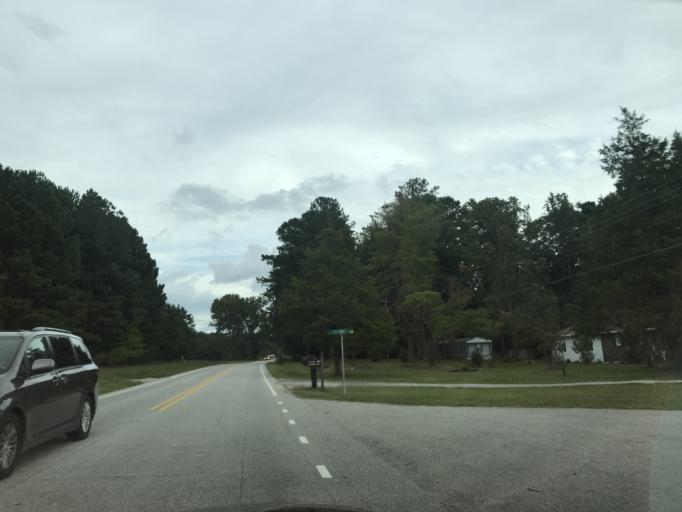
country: US
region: North Carolina
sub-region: Franklin County
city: Youngsville
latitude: 36.0019
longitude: -78.4289
